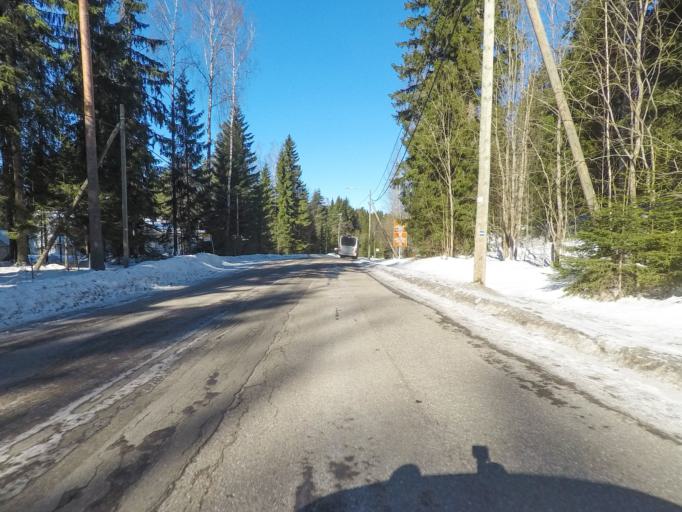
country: FI
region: Uusimaa
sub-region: Helsinki
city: Espoo
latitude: 60.3081
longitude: 24.5484
